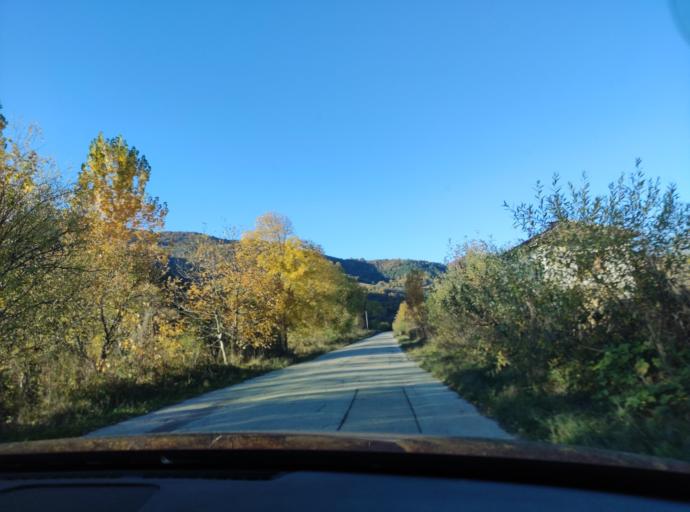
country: BG
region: Montana
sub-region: Obshtina Chiprovtsi
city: Chiprovtsi
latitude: 43.3879
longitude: 22.9223
